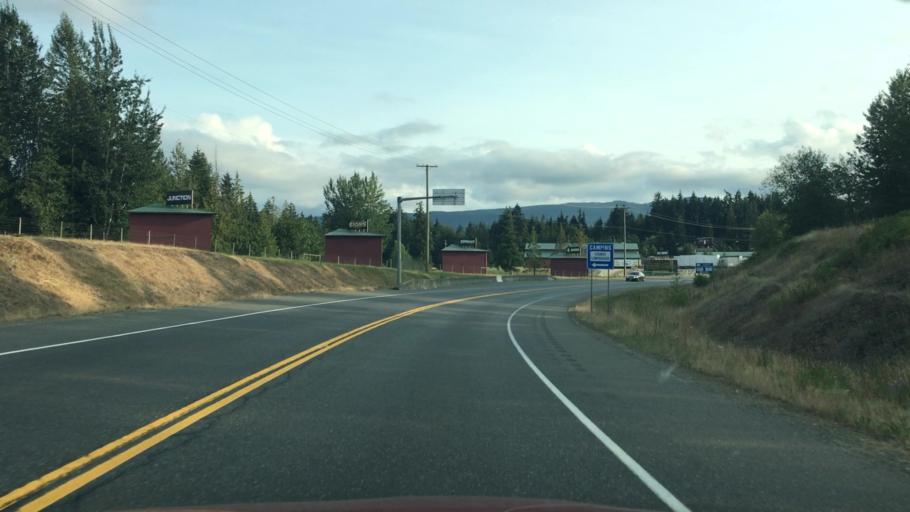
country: CA
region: British Columbia
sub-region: Regional District of Nanaimo
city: Parksville
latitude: 49.3060
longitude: -124.4501
